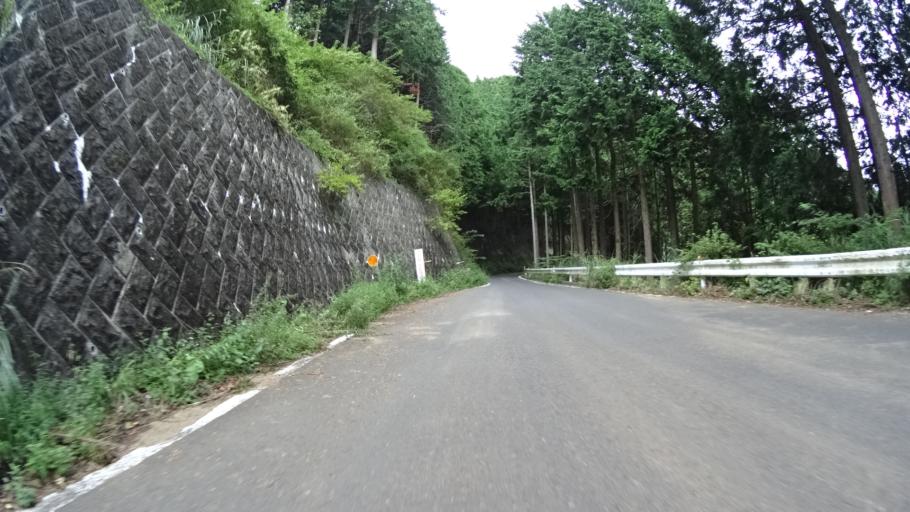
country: JP
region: Kanagawa
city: Hadano
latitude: 35.4208
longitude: 139.2142
